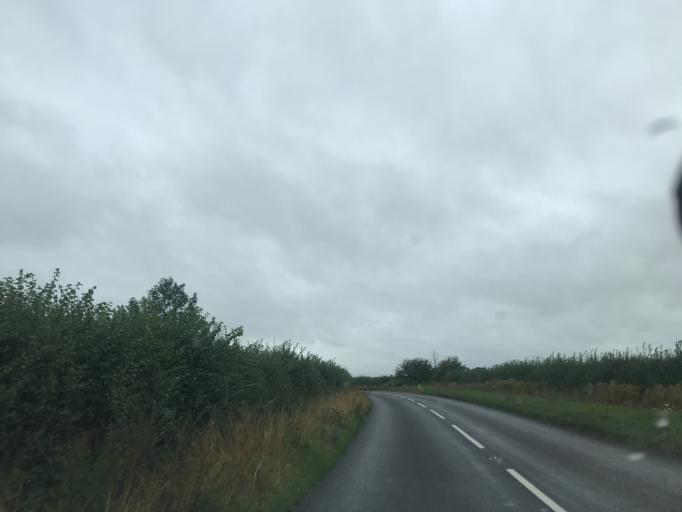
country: GB
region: England
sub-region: Buckinghamshire
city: Stone
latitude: 51.7901
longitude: -0.8674
